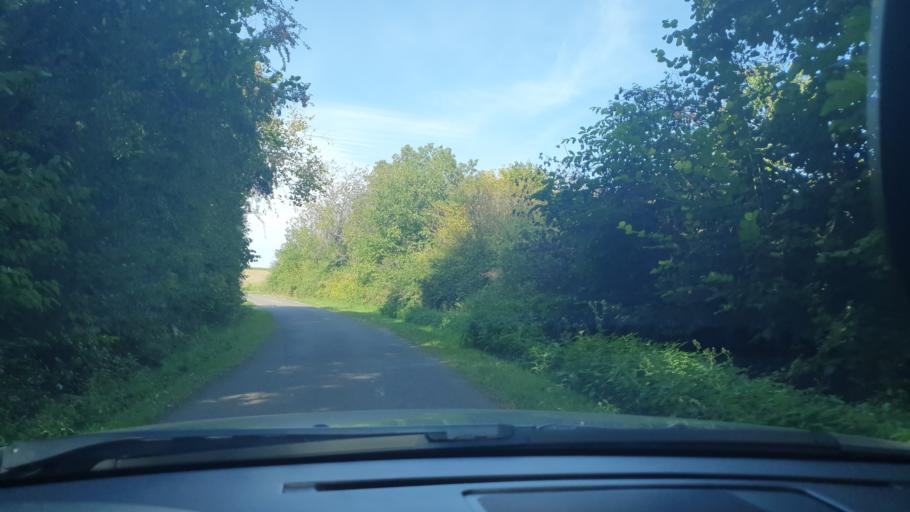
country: DE
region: Rheinland-Pfalz
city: Zweibrucken
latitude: 49.2691
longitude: 7.3821
